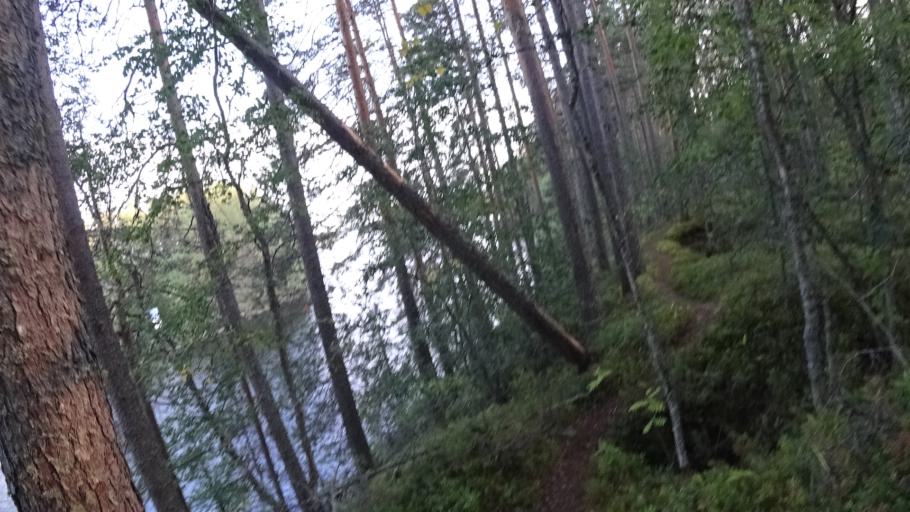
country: FI
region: North Karelia
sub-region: Joensuu
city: Ilomantsi
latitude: 62.5844
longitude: 31.1876
